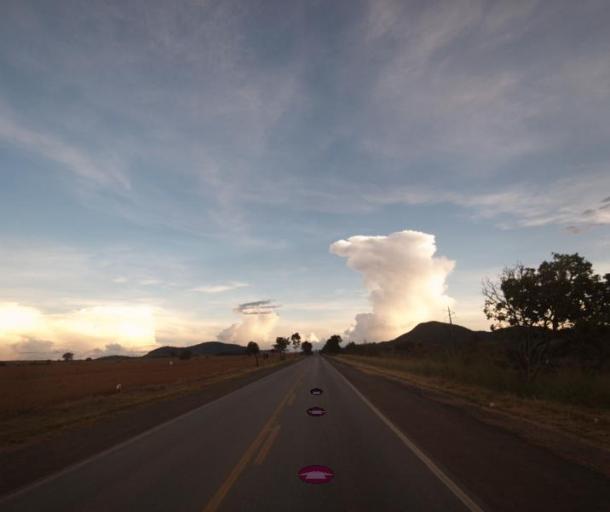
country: BR
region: Goias
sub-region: Uruacu
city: Uruacu
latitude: -14.3665
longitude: -49.1583
